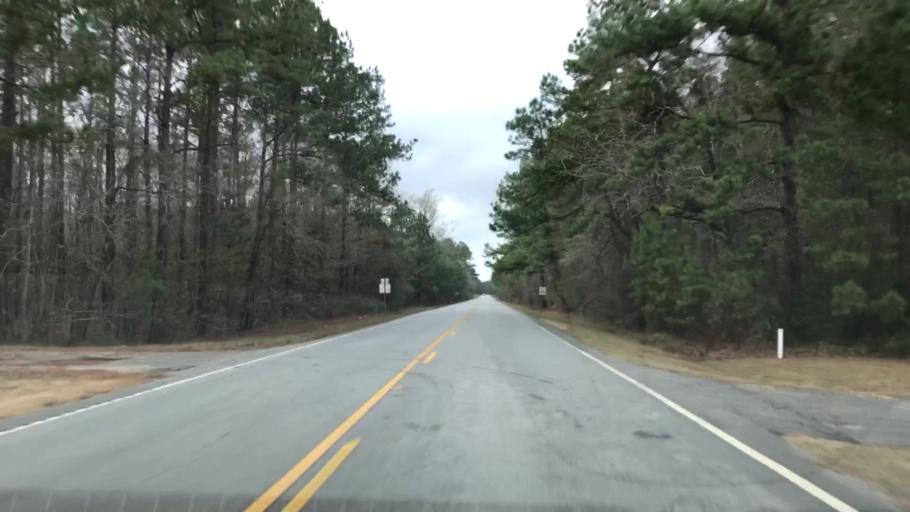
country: US
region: South Carolina
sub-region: Berkeley County
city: Saint Stephen
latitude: 33.2869
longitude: -79.7580
